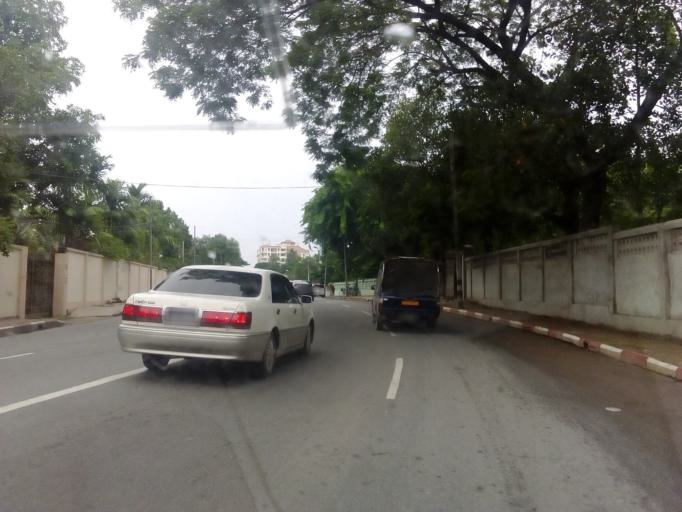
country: MM
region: Yangon
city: Yangon
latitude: 16.8541
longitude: 96.1468
